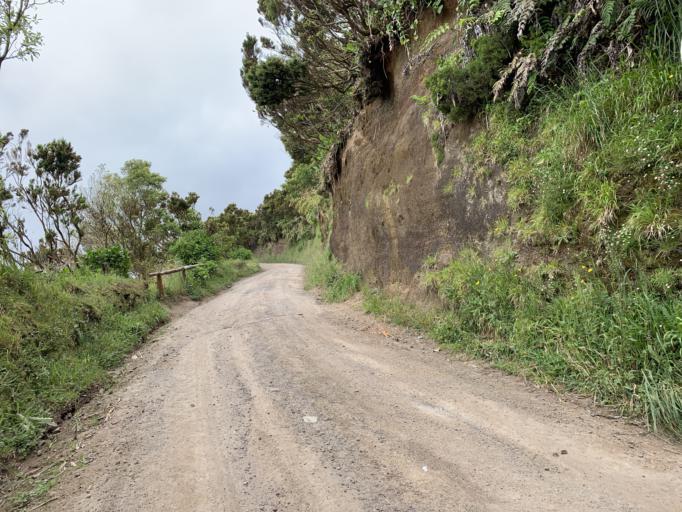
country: PT
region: Azores
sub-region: Ponta Delgada
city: Arrifes
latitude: 37.8722
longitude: -25.8118
